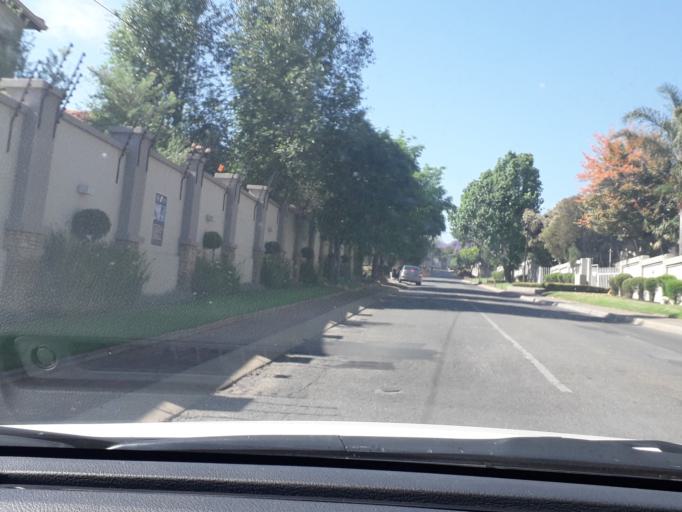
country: ZA
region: Gauteng
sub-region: City of Johannesburg Metropolitan Municipality
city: Modderfontein
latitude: -26.0859
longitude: 28.0514
